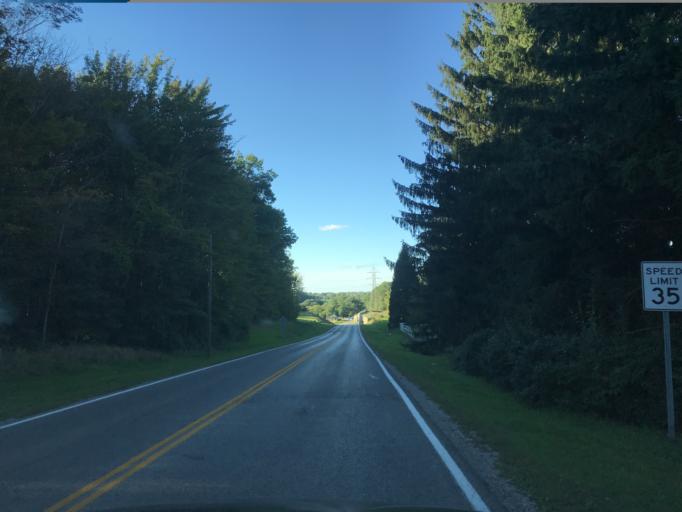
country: US
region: Ohio
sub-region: Ashtabula County
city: Edgewood
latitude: 41.8525
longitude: -80.7567
